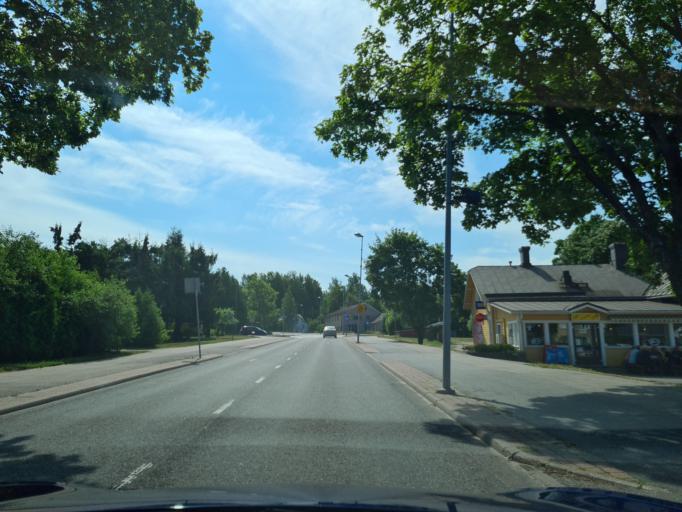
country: FI
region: Varsinais-Suomi
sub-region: Turku
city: Paimio
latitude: 60.4514
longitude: 22.6935
